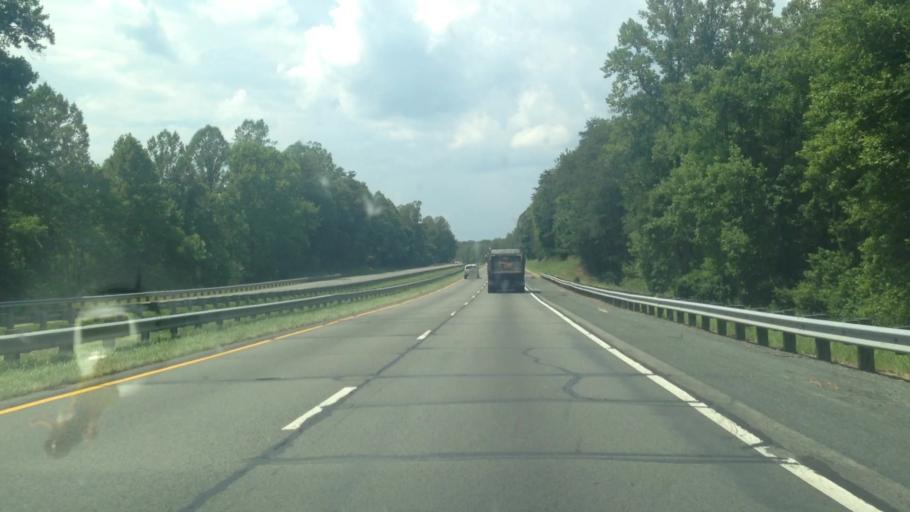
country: US
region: North Carolina
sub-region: Stokes County
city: King
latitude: 36.2919
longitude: -80.4040
